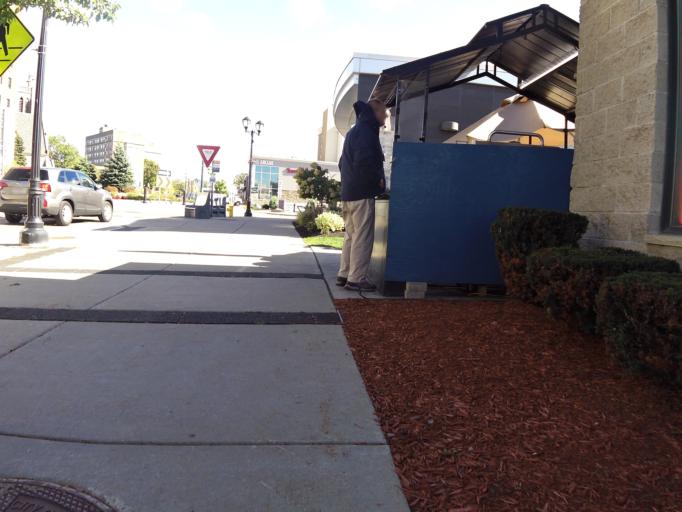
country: US
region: New York
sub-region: Niagara County
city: Niagara Falls
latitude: 43.0847
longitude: -79.0622
